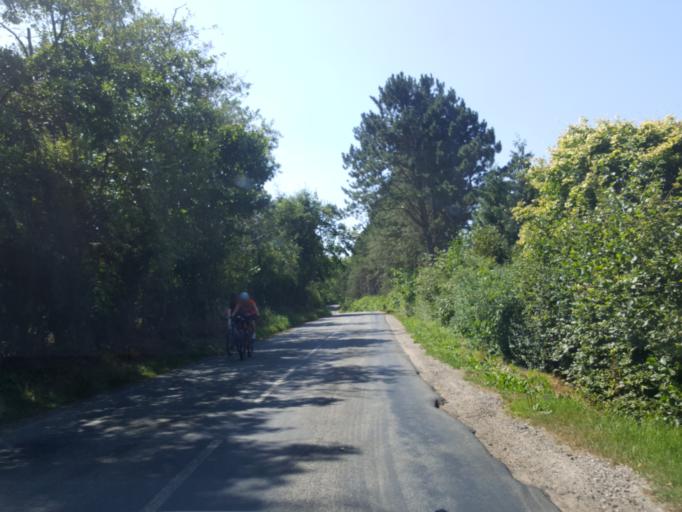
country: DK
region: Capital Region
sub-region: Fredensborg Kommune
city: Kokkedal
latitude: 55.9257
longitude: 12.4610
